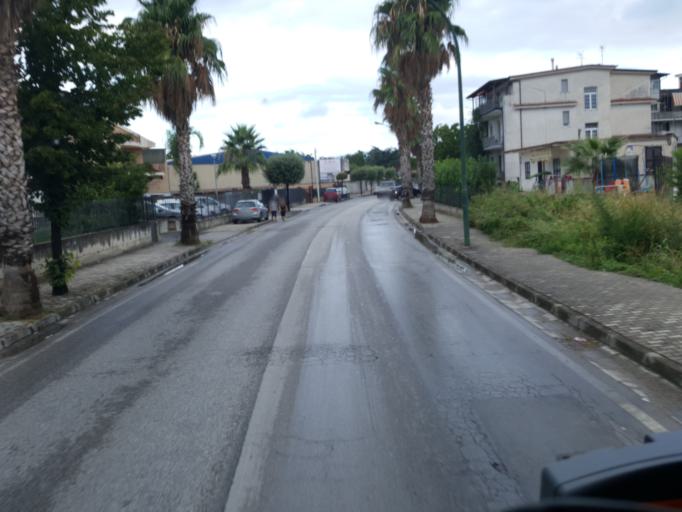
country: IT
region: Campania
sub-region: Provincia di Napoli
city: Palma Campania
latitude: 40.8608
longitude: 14.5488
